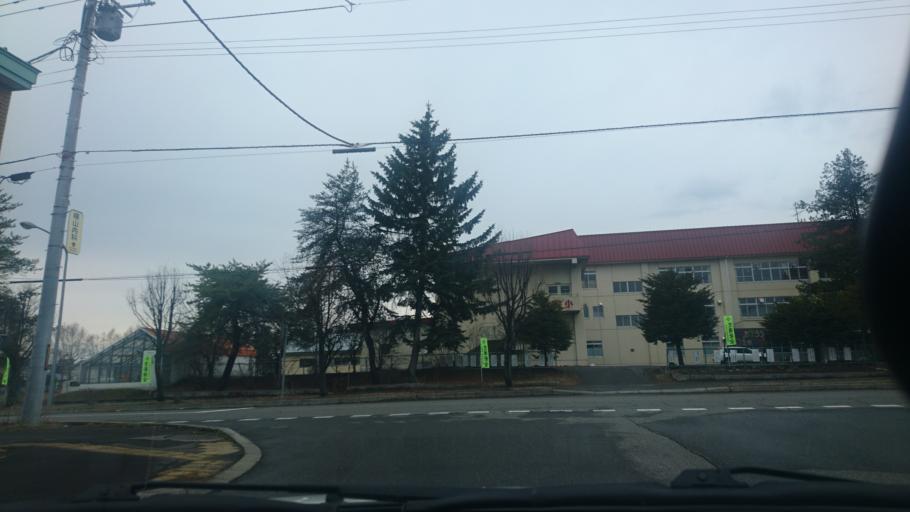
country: JP
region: Hokkaido
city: Obihiro
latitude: 42.9301
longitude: 143.1934
